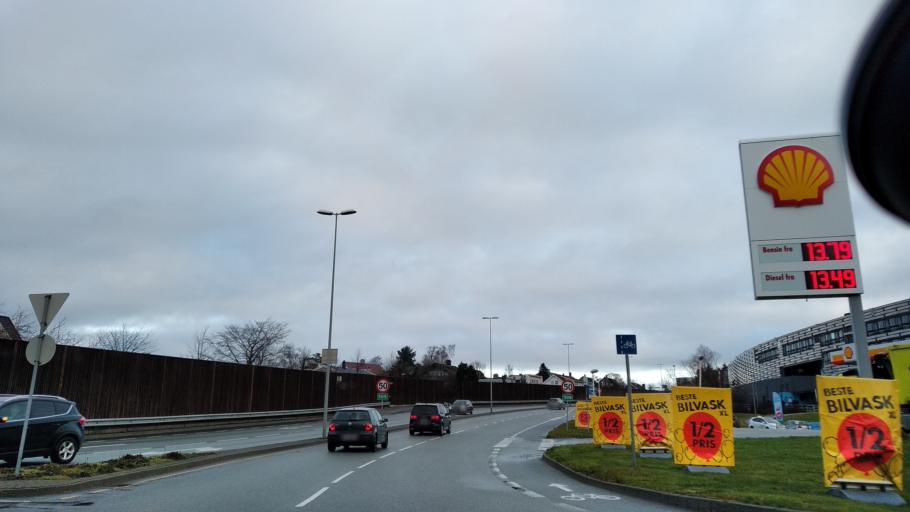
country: NO
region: Rogaland
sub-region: Stavanger
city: Stavanger
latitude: 58.9527
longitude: 5.6756
